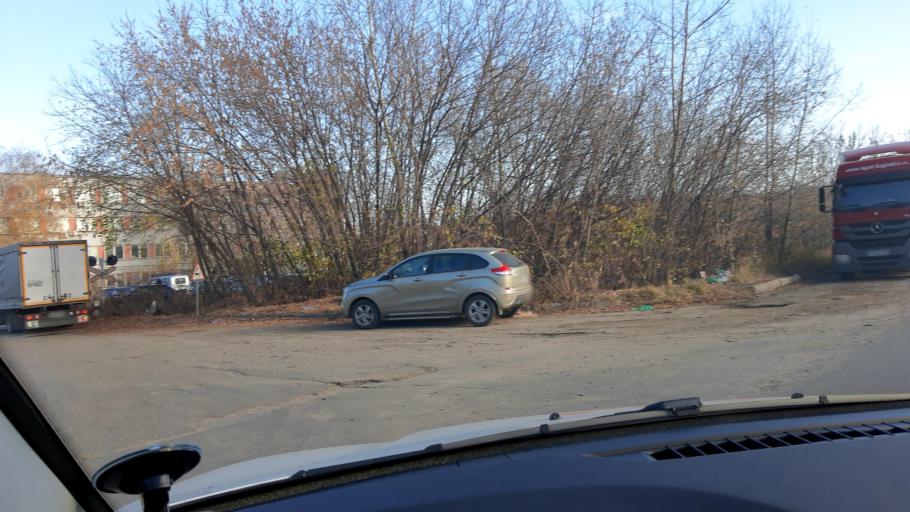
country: RU
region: Nizjnij Novgorod
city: Nizhniy Novgorod
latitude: 56.2418
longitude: 43.9040
